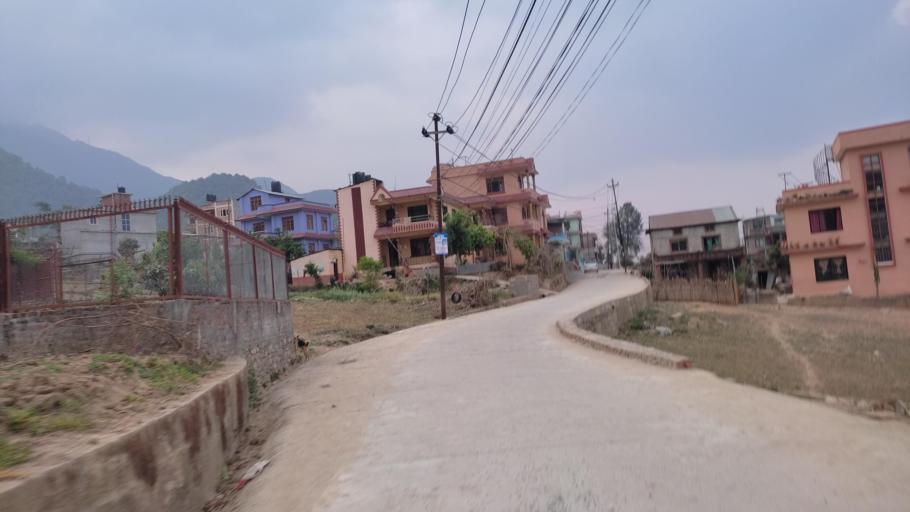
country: NP
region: Central Region
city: Kirtipur
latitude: 27.6694
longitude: 85.2454
